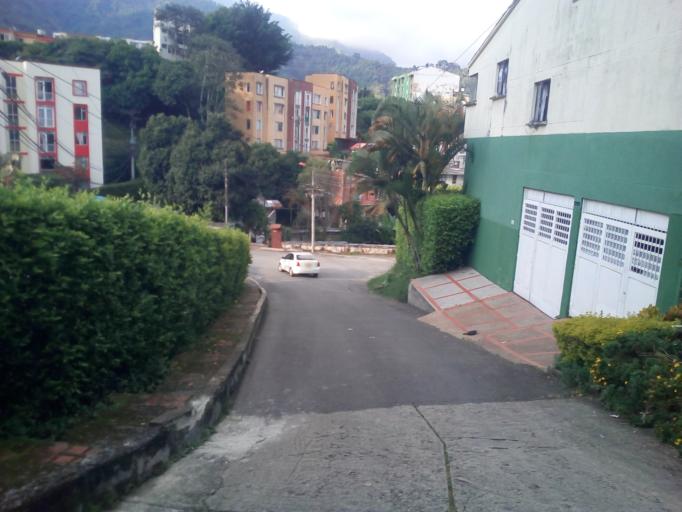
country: CO
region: Tolima
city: Ibague
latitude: 4.4500
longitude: -75.2471
